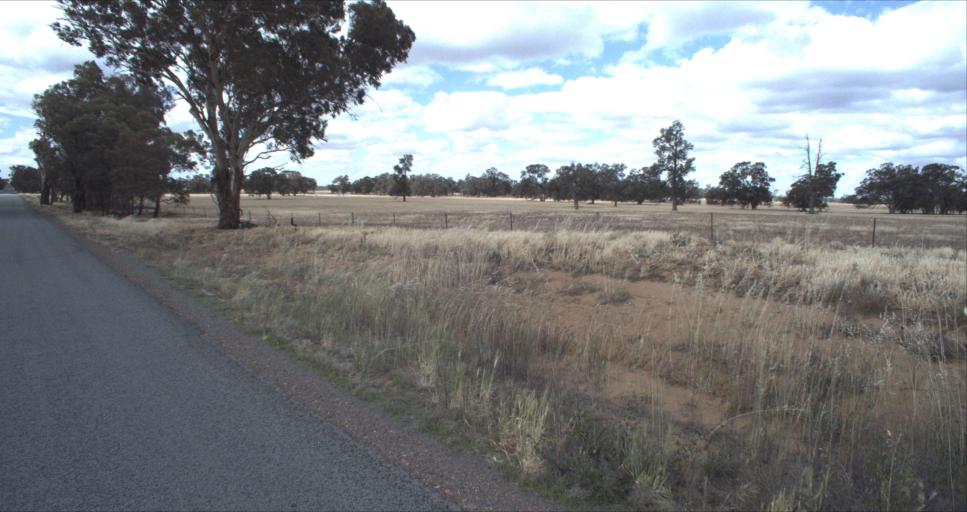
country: AU
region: New South Wales
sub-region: Leeton
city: Leeton
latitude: -34.6724
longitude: 146.3472
